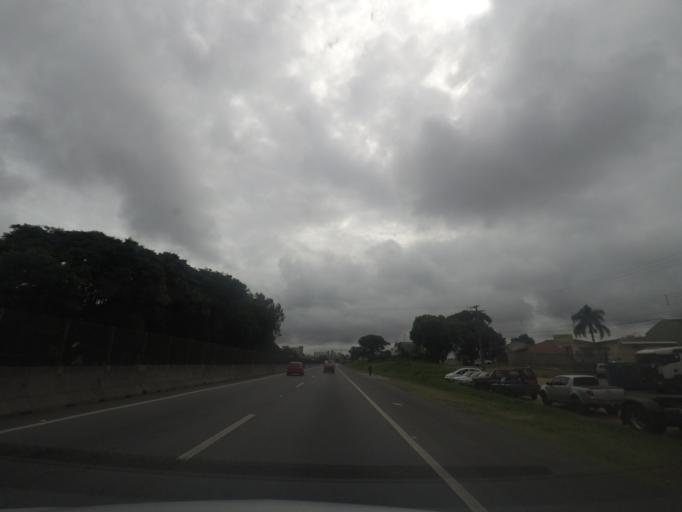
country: BR
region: Parana
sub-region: Pinhais
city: Pinhais
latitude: -25.4559
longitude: -49.2237
